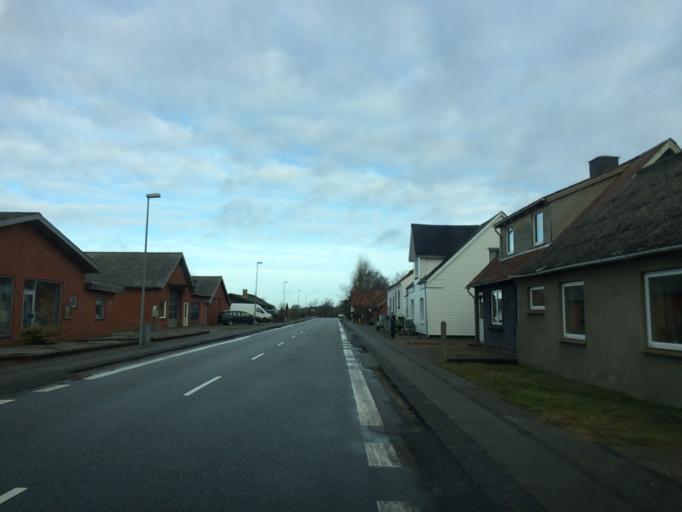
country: DK
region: Central Jutland
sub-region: Struer Kommune
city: Struer
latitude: 56.4724
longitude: 8.5486
